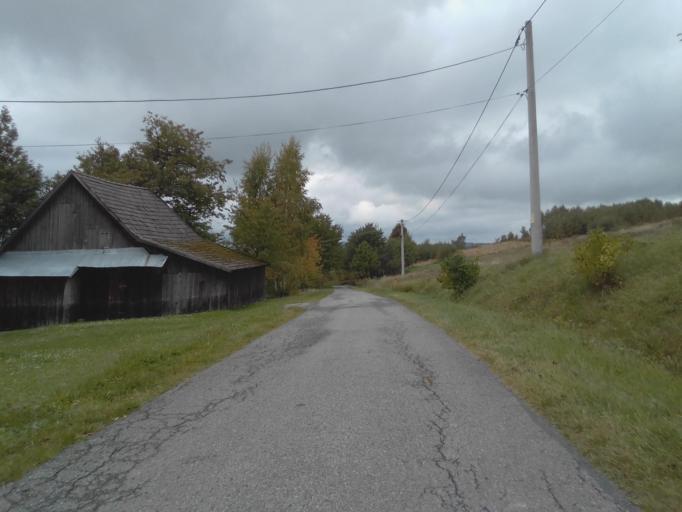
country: PL
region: Subcarpathian Voivodeship
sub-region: Powiat strzyzowski
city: Gwoznica Gorna
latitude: 49.8344
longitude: 22.0162
